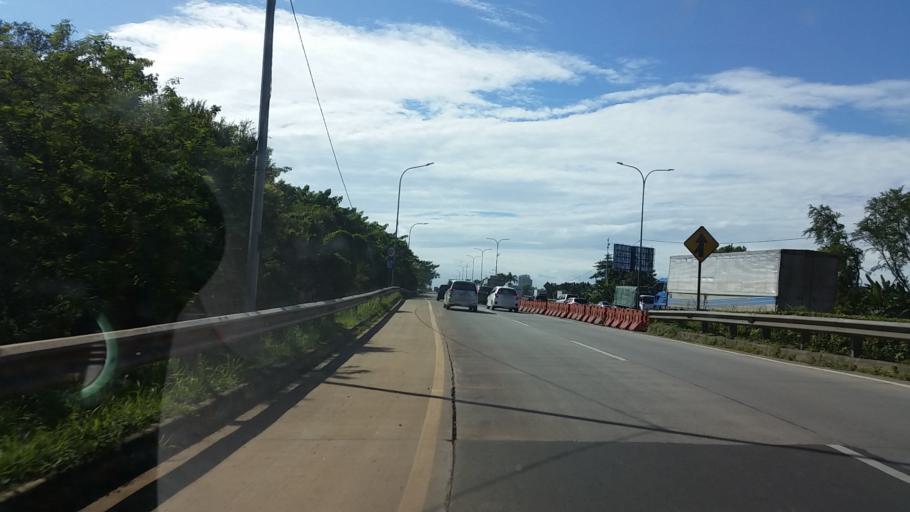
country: ID
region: Banten
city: South Tangerang
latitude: -6.2521
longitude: 106.7641
